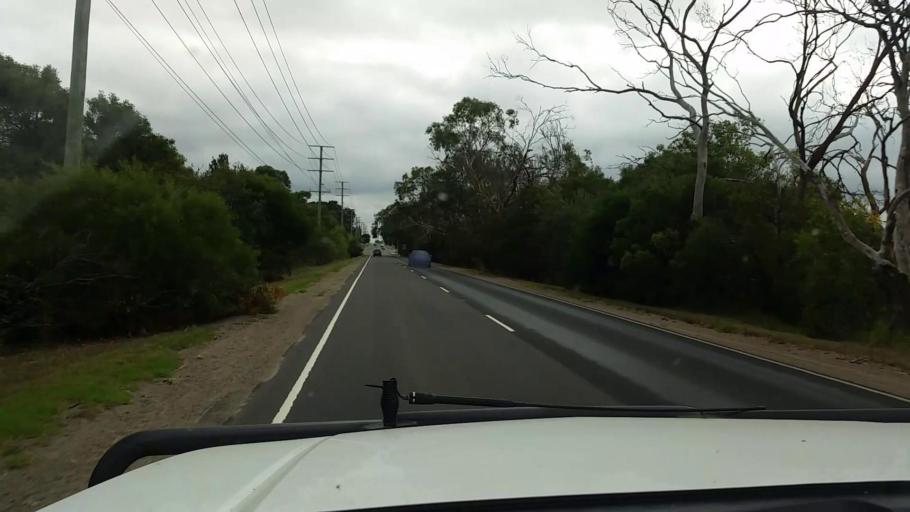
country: AU
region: Victoria
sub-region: Mornington Peninsula
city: Tyabb
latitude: -38.2680
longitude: 145.1898
